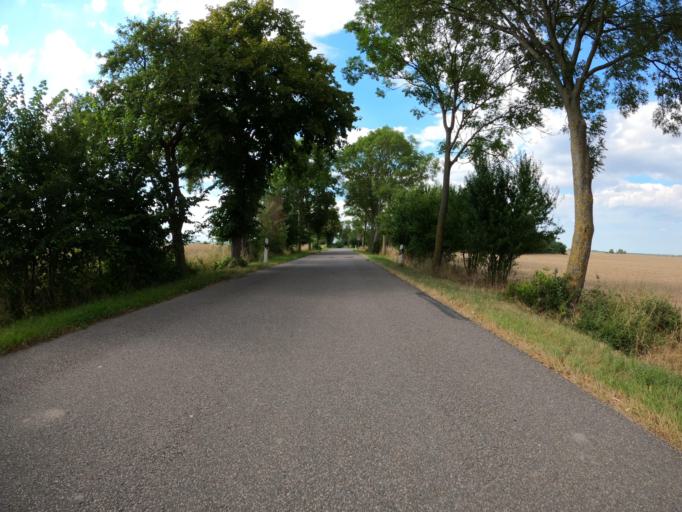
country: DE
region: Mecklenburg-Vorpommern
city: Woldegk
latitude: 53.4349
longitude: 13.5999
